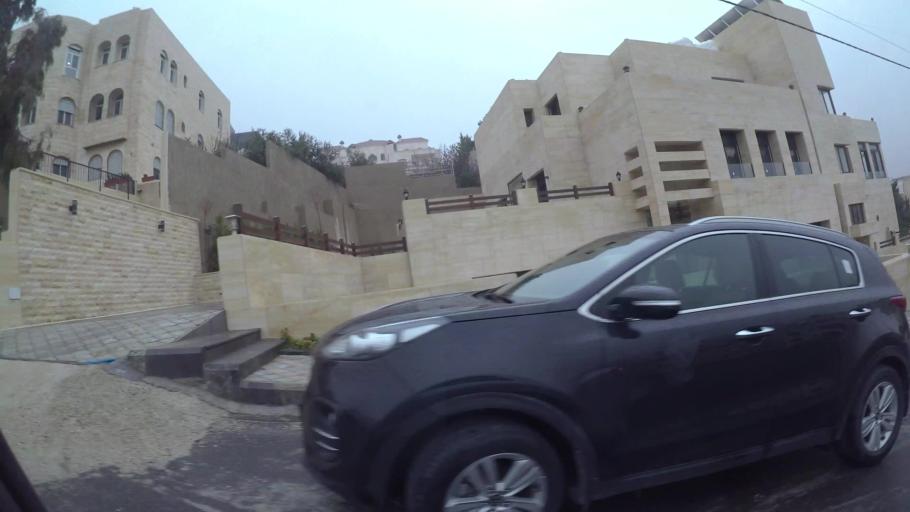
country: JO
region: Amman
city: Al Jubayhah
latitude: 32.0144
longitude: 35.8349
